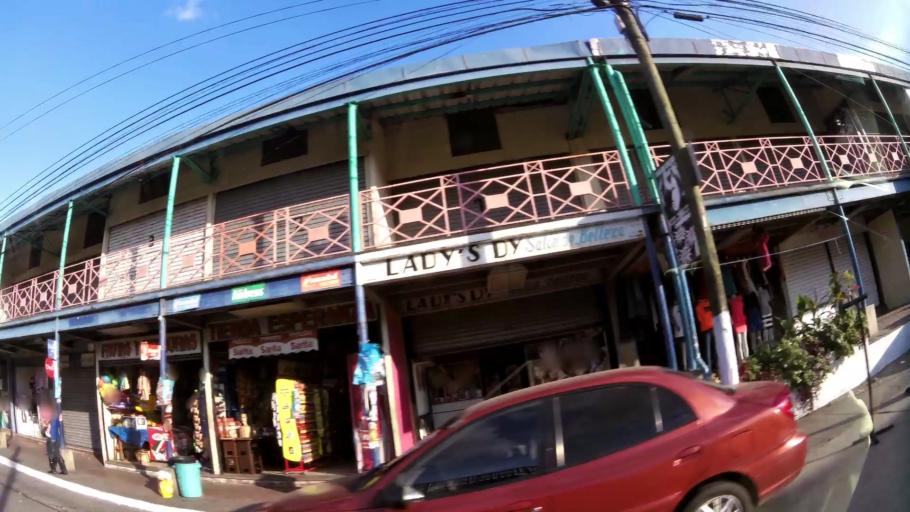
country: GT
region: Guatemala
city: Villa Nueva
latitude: 14.5195
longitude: -90.5794
